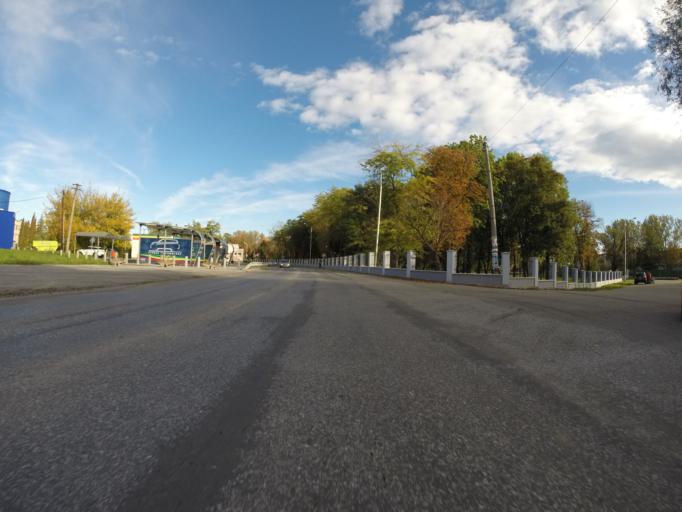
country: SK
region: Banskobystricky
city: Rimavska Sobota
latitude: 48.3856
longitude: 20.0029
